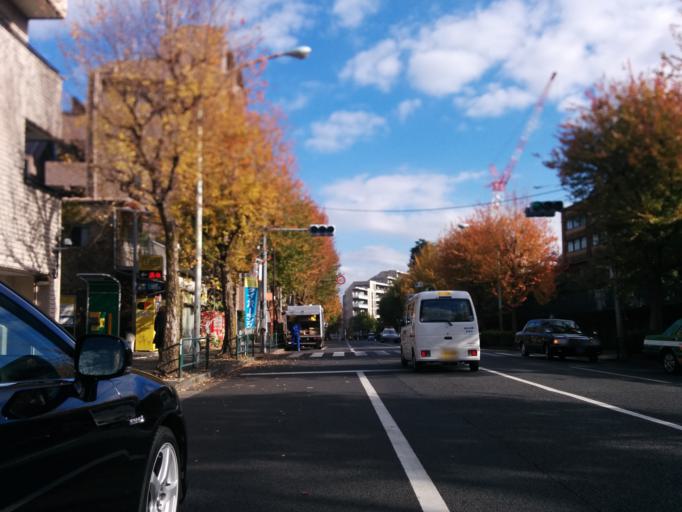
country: JP
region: Tokyo
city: Tokyo
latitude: 35.7078
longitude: 139.7134
